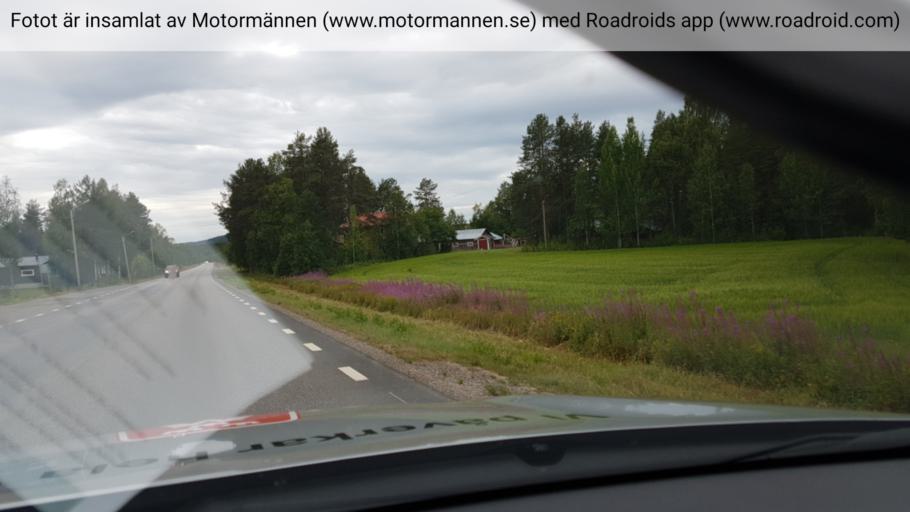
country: SE
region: Norrbotten
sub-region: Overkalix Kommun
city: OEverkalix
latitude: 66.3617
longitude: 22.8380
